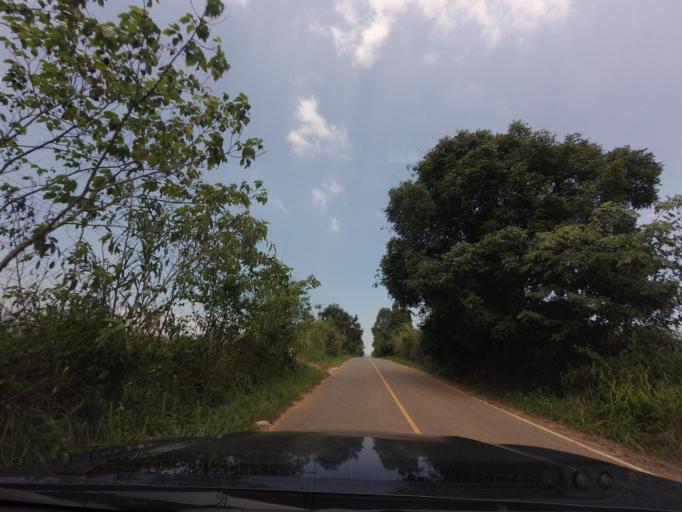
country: TH
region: Loei
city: Na Haeo
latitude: 17.5276
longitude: 100.8798
